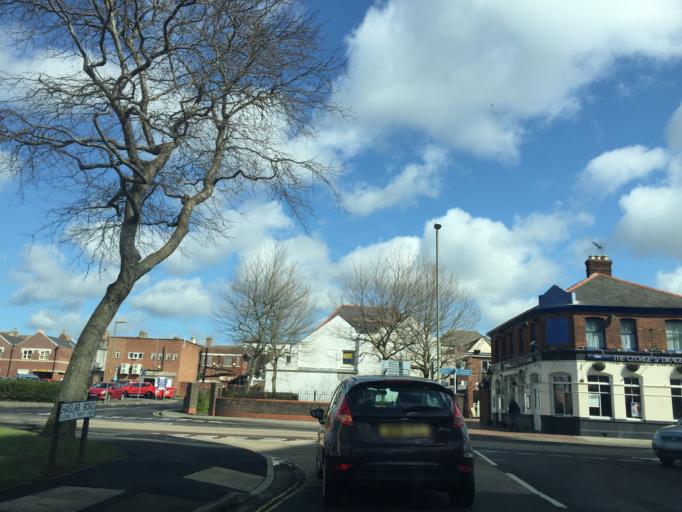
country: GB
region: England
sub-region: Hampshire
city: Gosport
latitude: 50.7941
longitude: -1.1209
